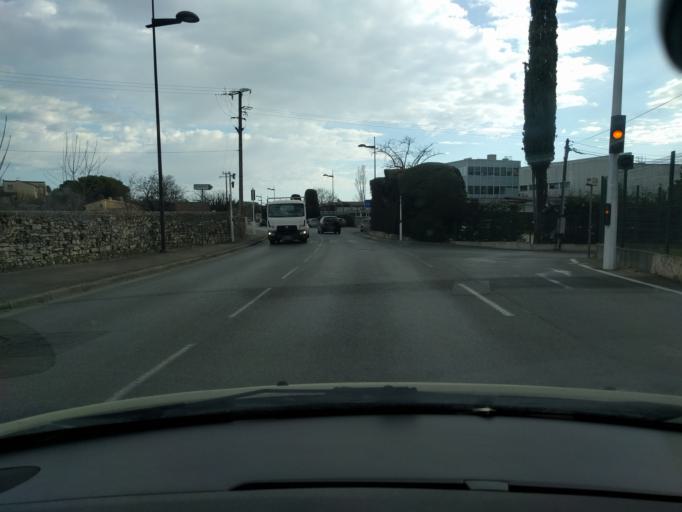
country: FR
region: Provence-Alpes-Cote d'Azur
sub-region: Departement des Alpes-Maritimes
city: Mouans-Sartoux
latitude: 43.6392
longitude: 6.9561
